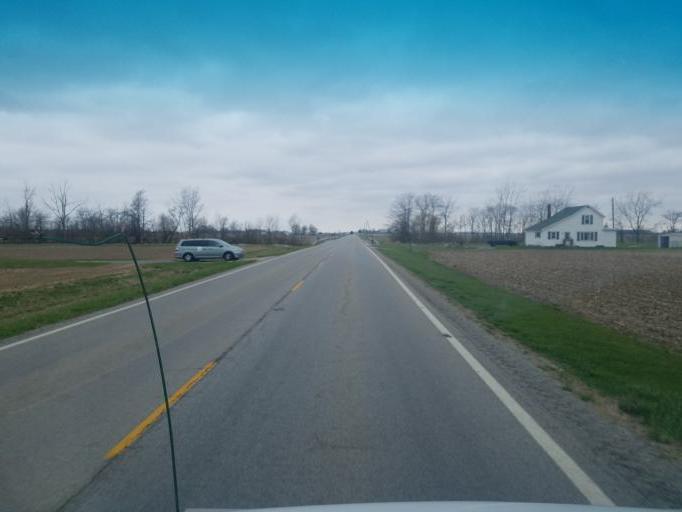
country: US
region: Ohio
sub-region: Allen County
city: Delphos
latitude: 40.9320
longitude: -84.4433
